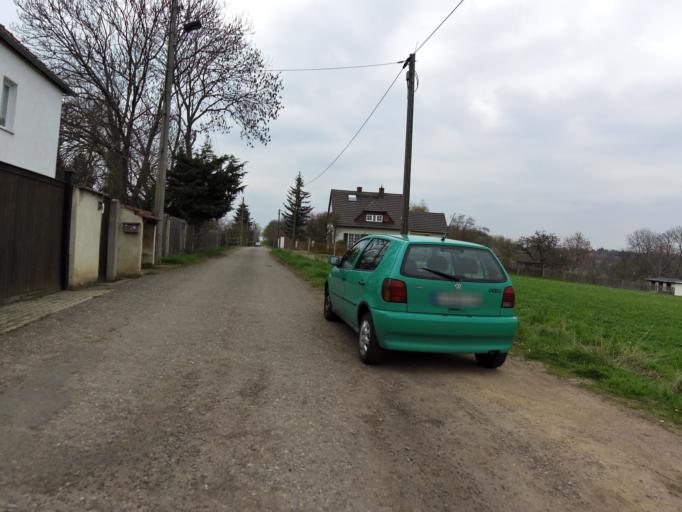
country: DE
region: Thuringia
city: Gotha
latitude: 50.9564
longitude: 10.7027
